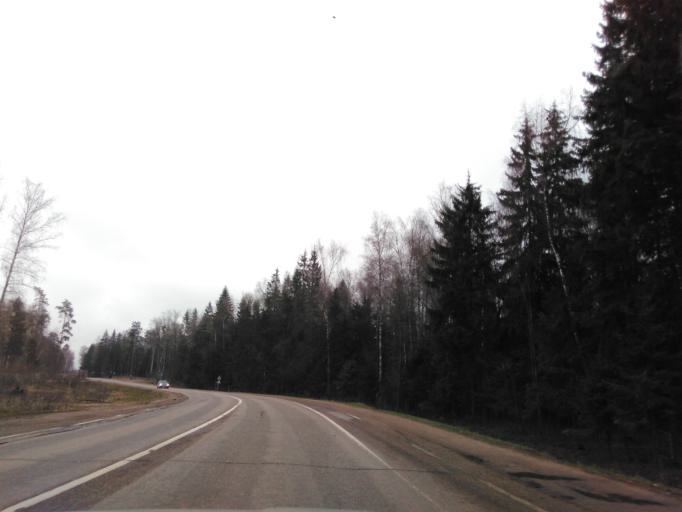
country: RU
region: Moskovskaya
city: Rozhdestveno
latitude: 55.8337
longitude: 37.0200
